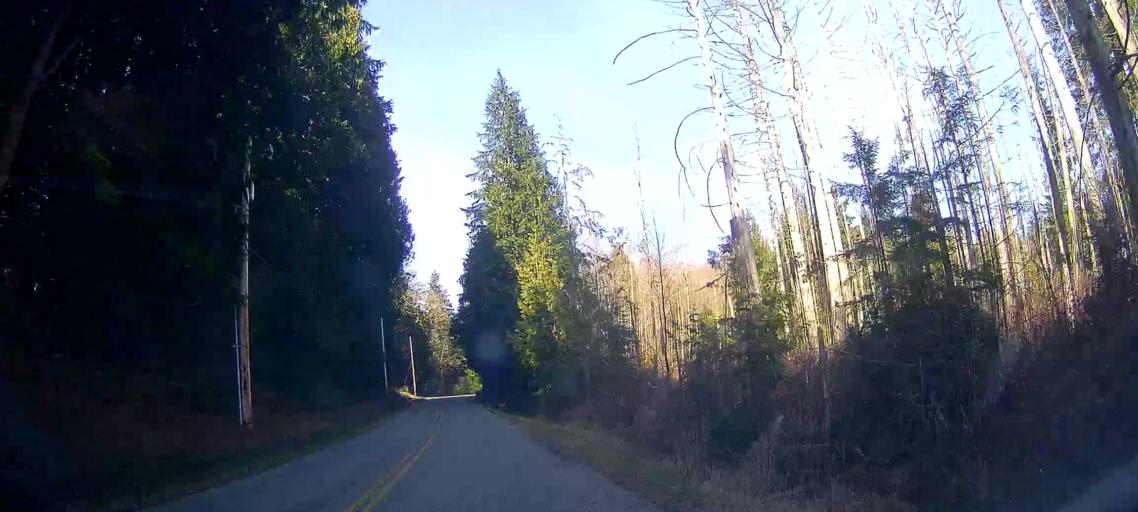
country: US
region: Washington
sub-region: Whatcom County
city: Sudden Valley
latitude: 48.6112
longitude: -122.3669
